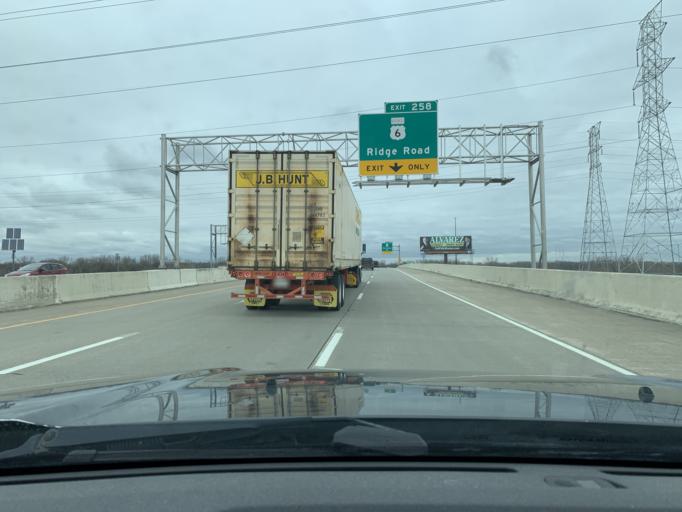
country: US
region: Indiana
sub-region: Lake County
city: New Chicago
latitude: 41.5651
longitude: -87.3046
